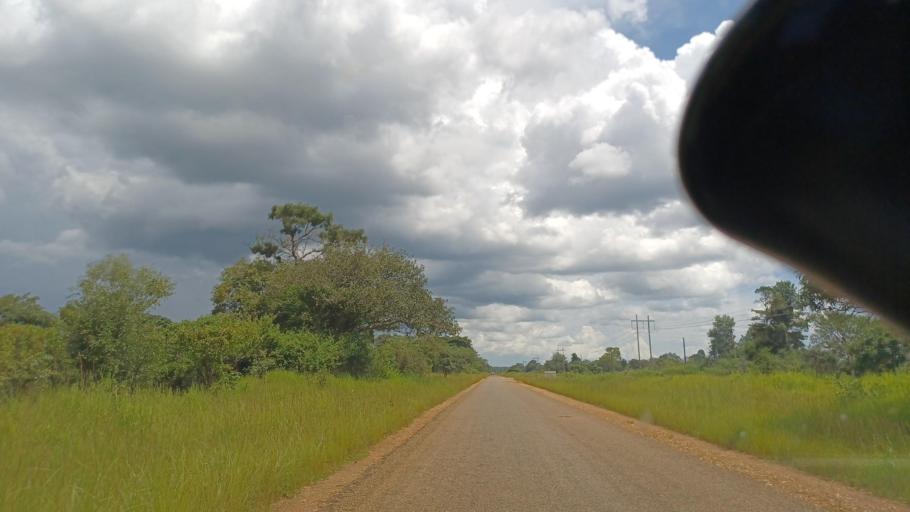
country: ZM
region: North-Western
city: Solwezi
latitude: -12.7620
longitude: 26.0208
